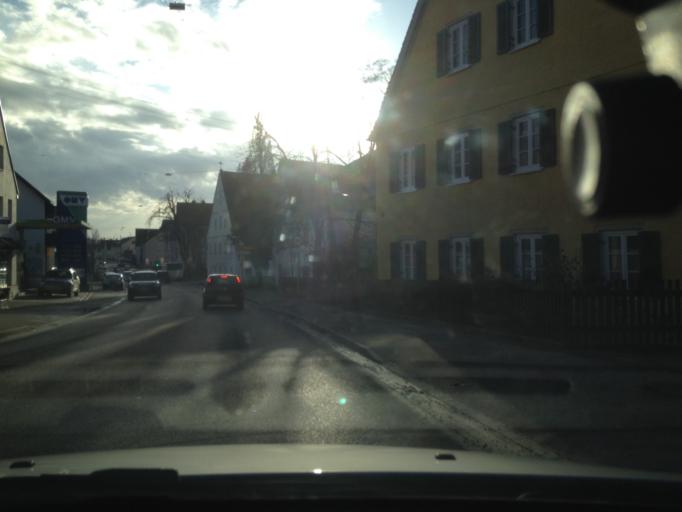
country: DE
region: Bavaria
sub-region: Swabia
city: Grossaitingen
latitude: 48.2279
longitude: 10.7808
